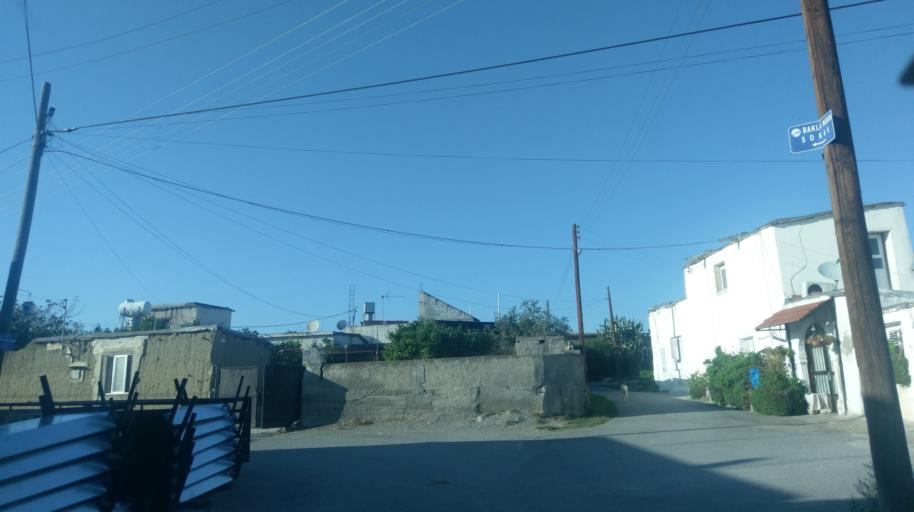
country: CY
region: Ammochostos
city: Lefkonoiko
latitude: 35.2830
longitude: 33.6872
